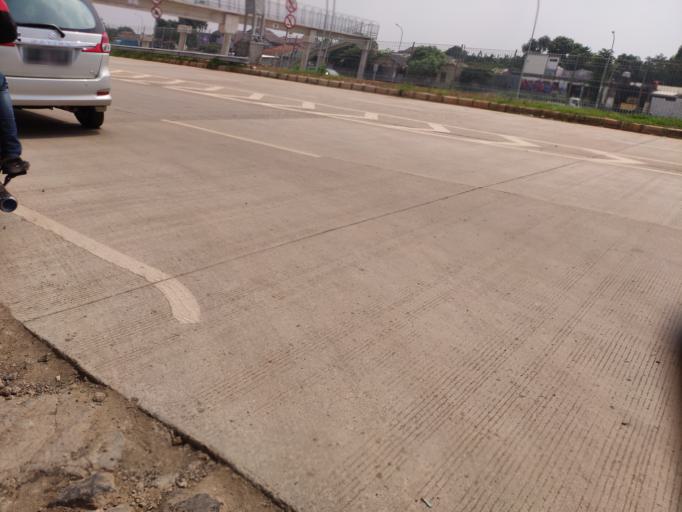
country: ID
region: West Java
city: Pamulang
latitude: -6.3217
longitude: 106.8030
